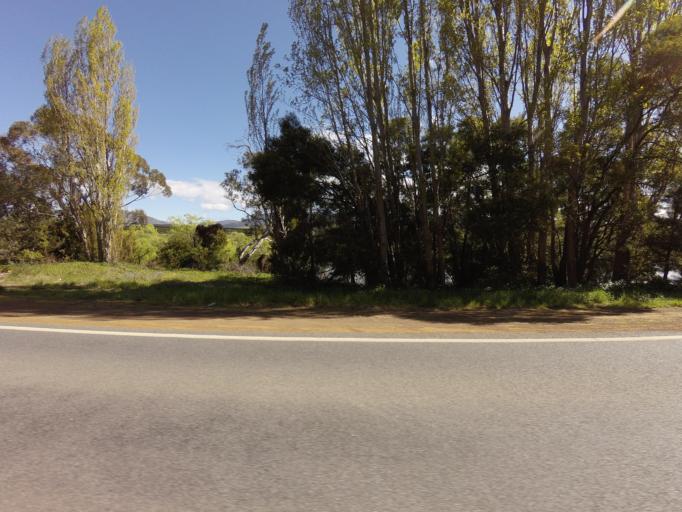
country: AU
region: Tasmania
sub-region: Derwent Valley
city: New Norfolk
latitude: -42.7356
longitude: 146.9760
